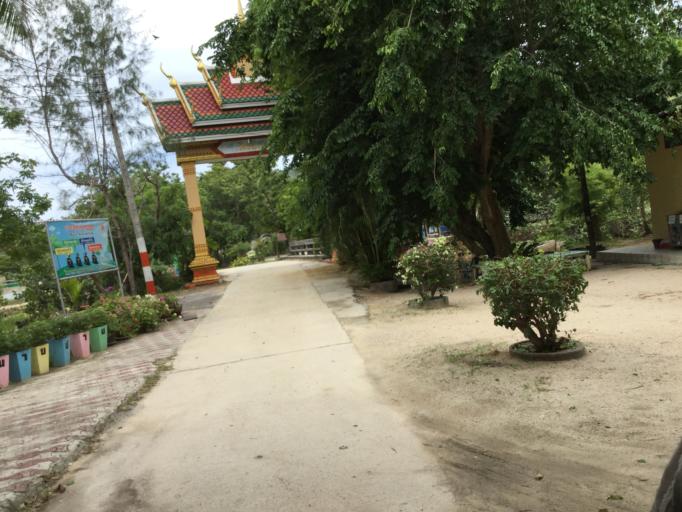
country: TH
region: Nakhon Si Thammarat
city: Ko Pha Ngan
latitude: 9.7710
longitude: 100.0554
